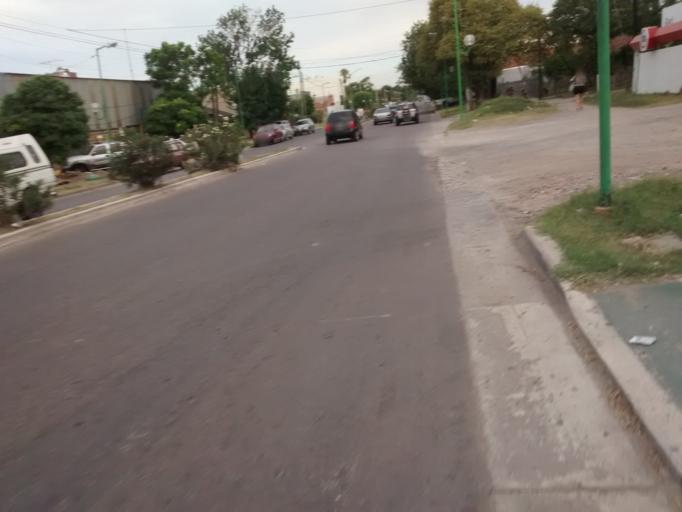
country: AR
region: Buenos Aires
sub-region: Partido de La Plata
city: La Plata
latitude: -34.9055
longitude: -58.0173
